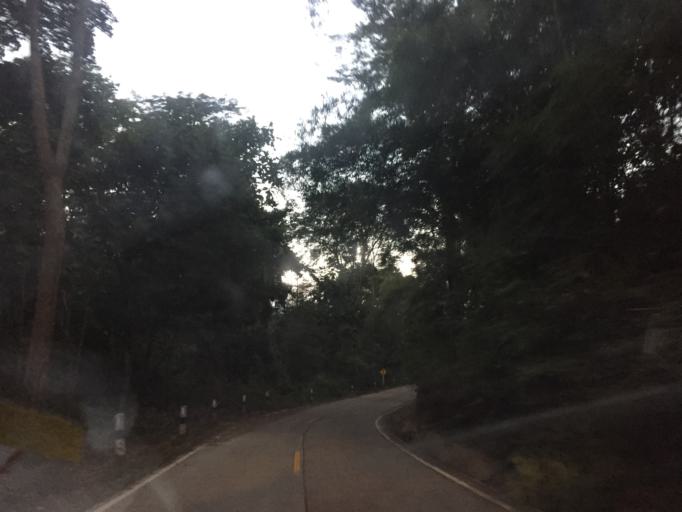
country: TH
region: Chiang Mai
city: Samoeng
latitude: 18.9953
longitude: 98.7179
